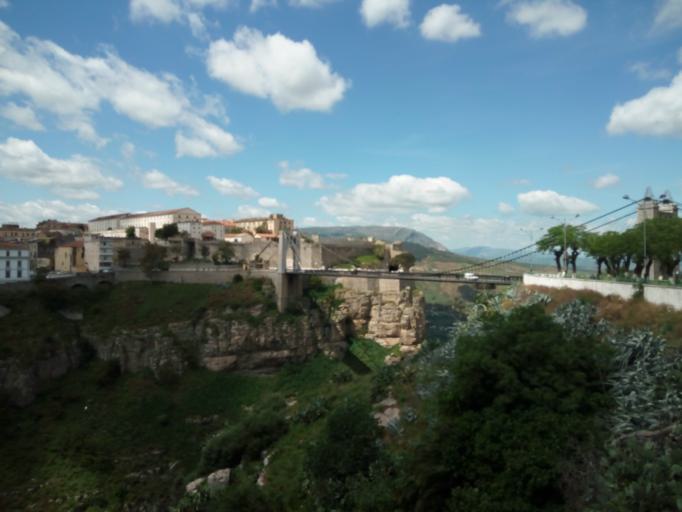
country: DZ
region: Constantine
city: Constantine
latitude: 36.3726
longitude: 6.6163
